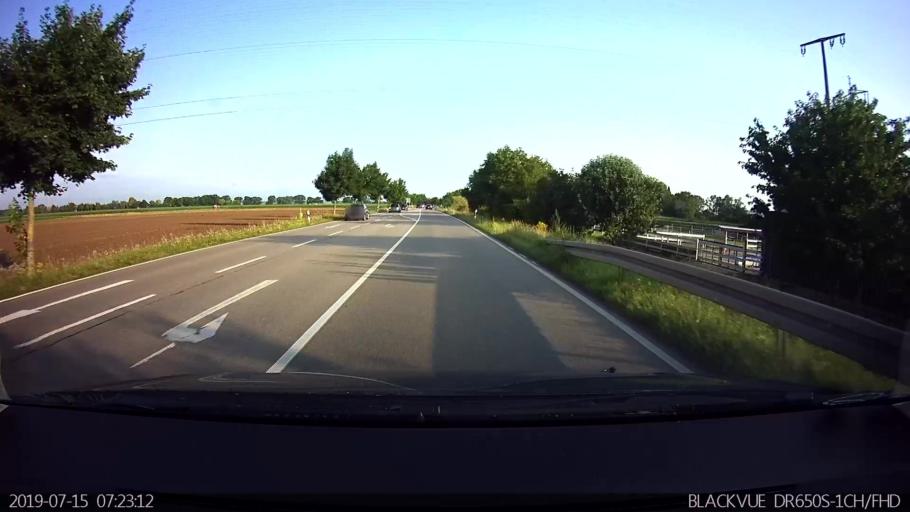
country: DE
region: Baden-Wuerttemberg
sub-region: Freiburg Region
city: Unterkrozingen
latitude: 47.9402
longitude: 7.6822
